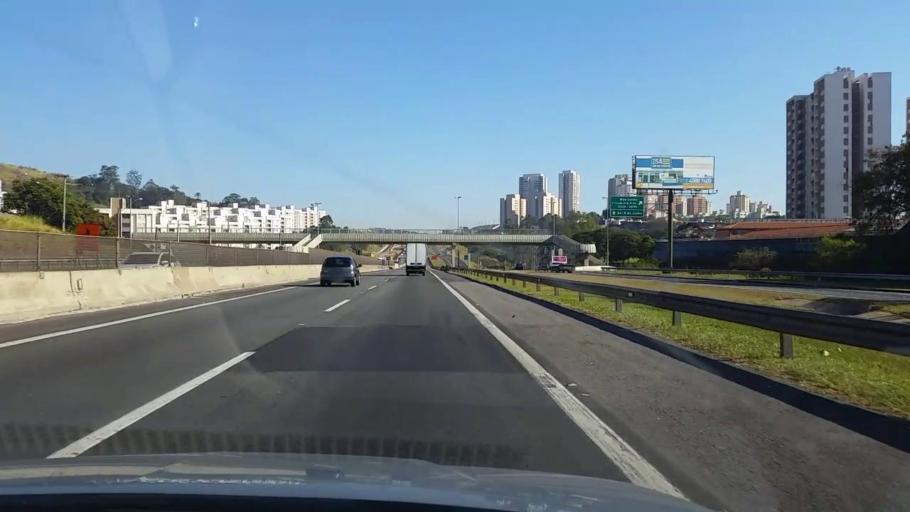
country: BR
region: Sao Paulo
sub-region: Jundiai
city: Jundiai
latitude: -23.2141
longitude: -46.8867
